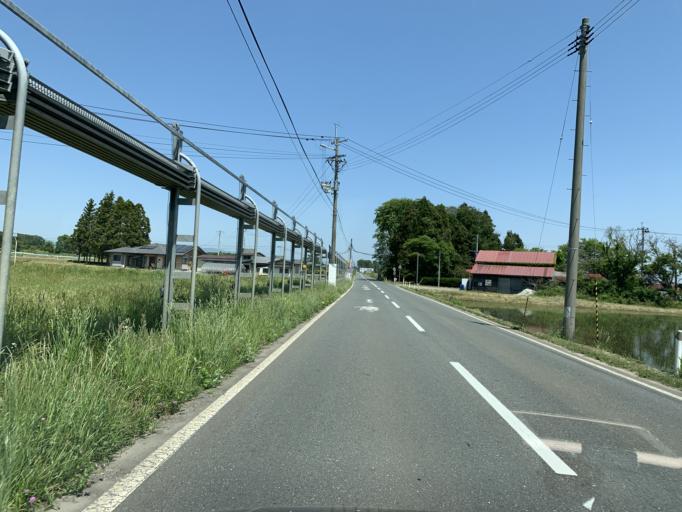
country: JP
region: Iwate
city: Kitakami
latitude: 39.2539
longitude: 141.0652
